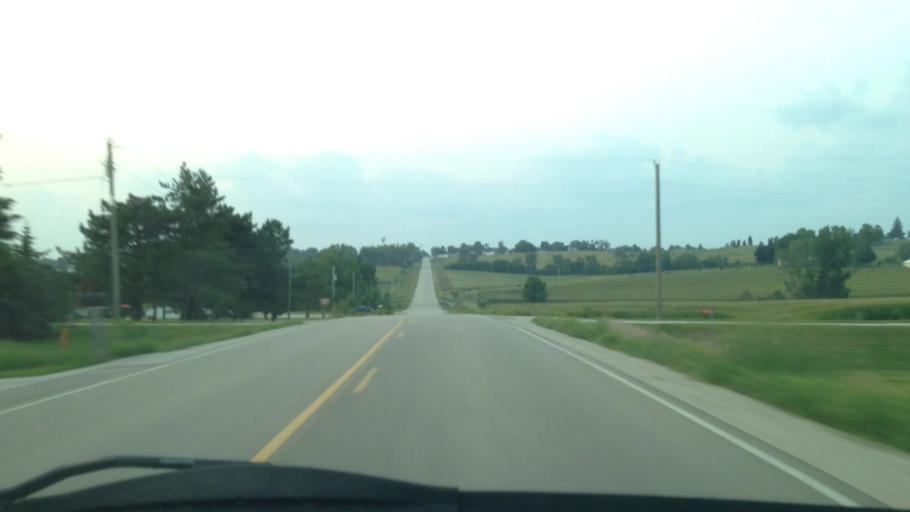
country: US
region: Iowa
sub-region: Benton County
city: Urbana
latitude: 42.2113
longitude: -91.8714
